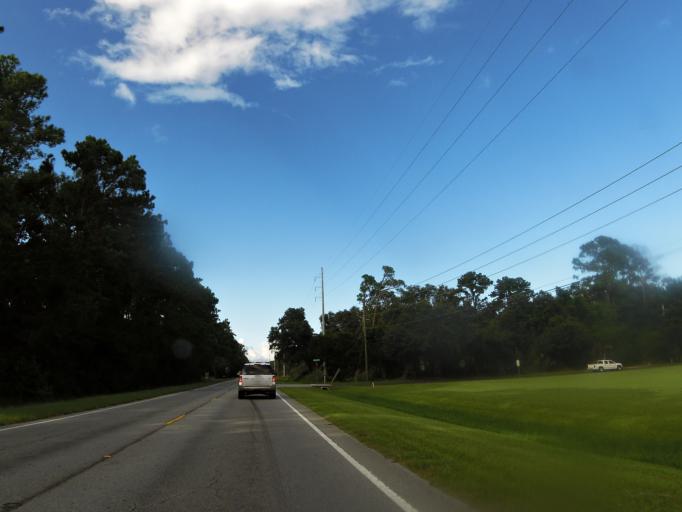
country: US
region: Georgia
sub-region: Glynn County
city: Country Club Estates
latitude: 31.2576
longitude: -81.4411
